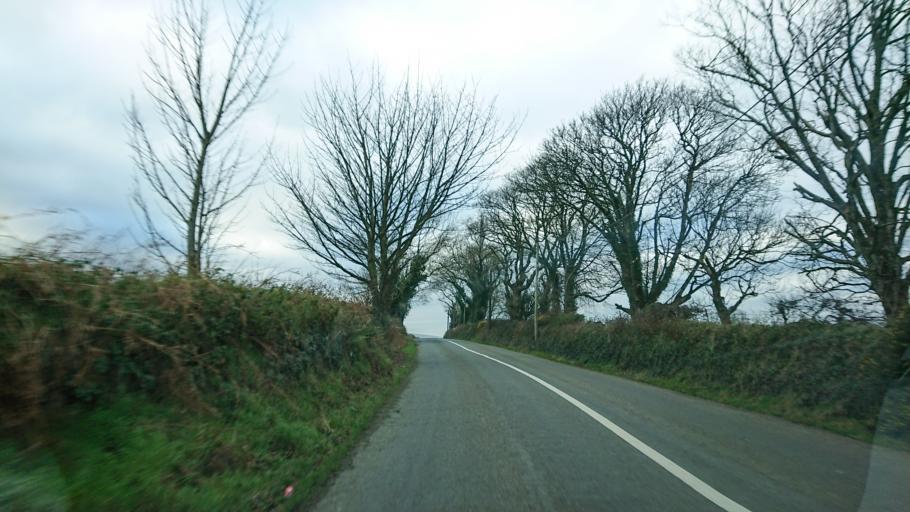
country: IE
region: Munster
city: Carrick-on-Suir
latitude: 52.3084
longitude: -7.5065
